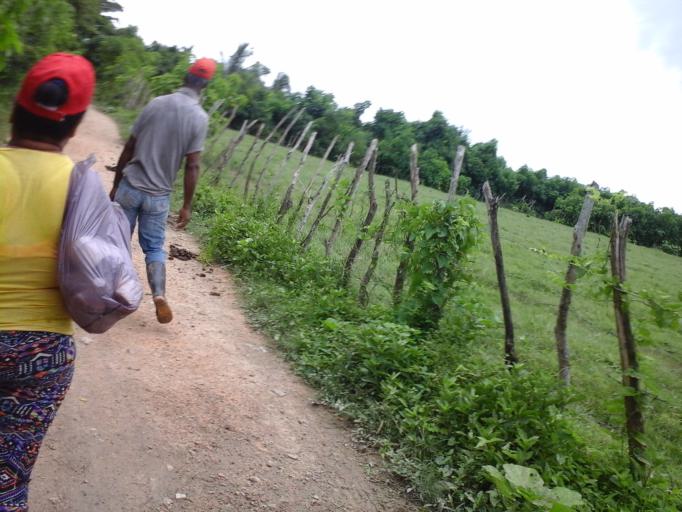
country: CO
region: Bolivar
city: San Pablo
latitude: 10.1528
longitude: -75.2732
